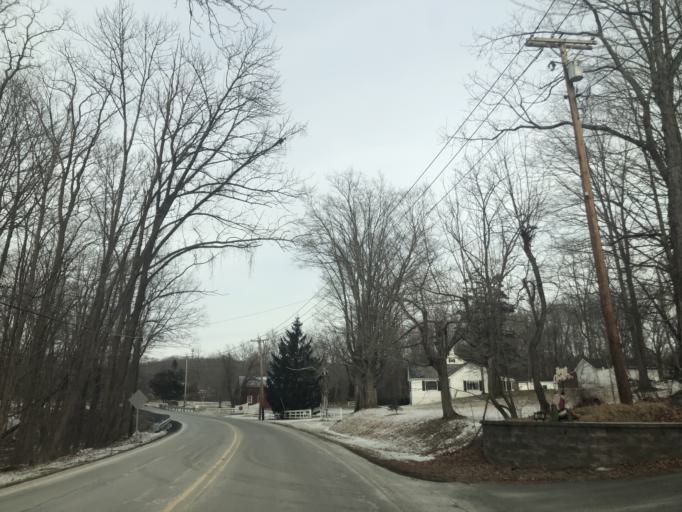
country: US
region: New Jersey
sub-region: Warren County
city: Oxford
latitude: 40.9281
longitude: -74.9995
